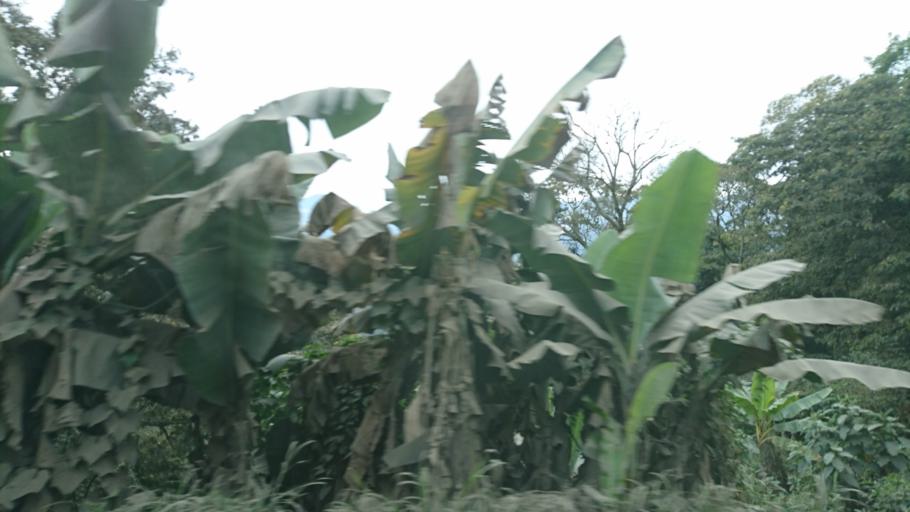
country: BO
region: La Paz
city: Coroico
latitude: -16.1992
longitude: -67.7028
